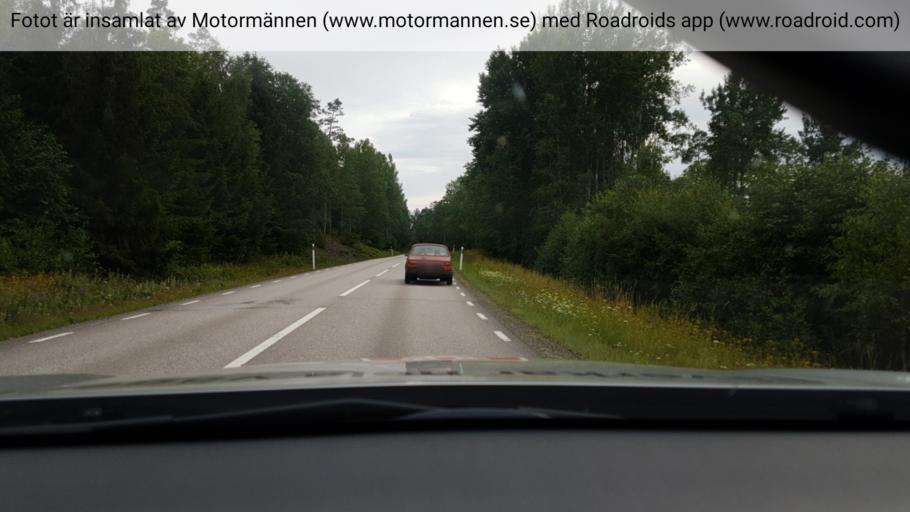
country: SE
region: Vaestra Goetaland
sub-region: Bengtsfors Kommun
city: Dals Langed
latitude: 58.9075
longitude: 12.2195
